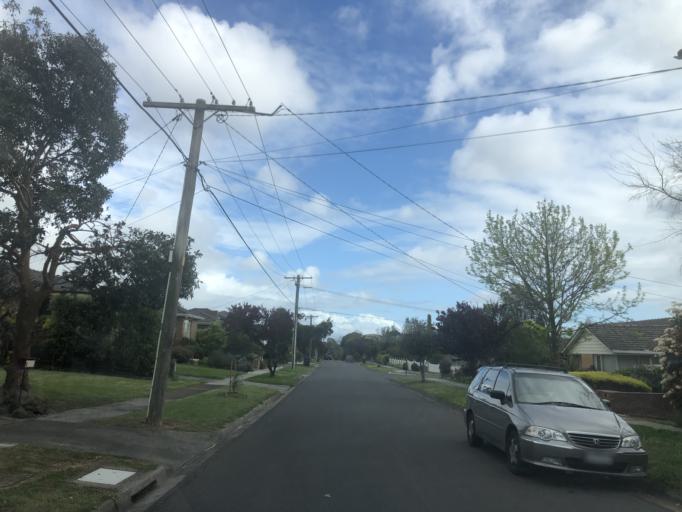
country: AU
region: Victoria
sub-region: Monash
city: Ashwood
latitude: -37.8799
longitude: 145.1200
